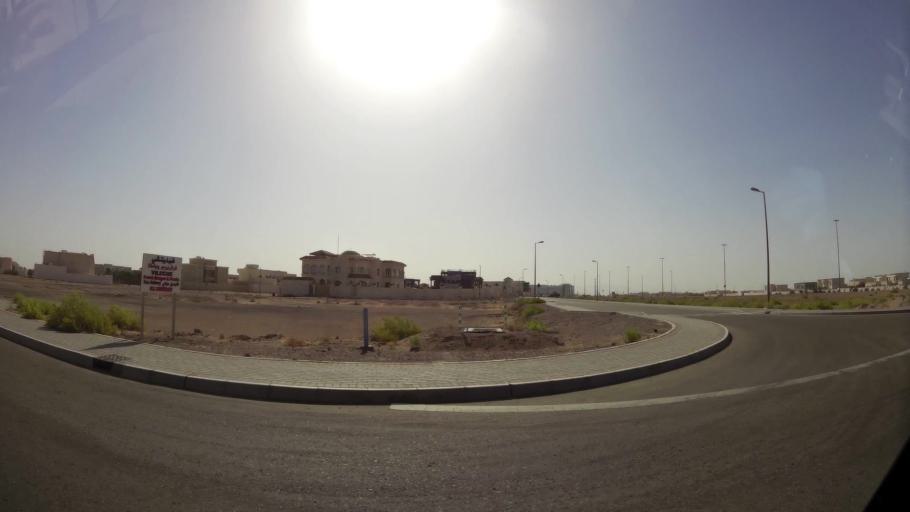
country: OM
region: Al Buraimi
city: Al Buraymi
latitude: 24.3456
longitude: 55.7836
